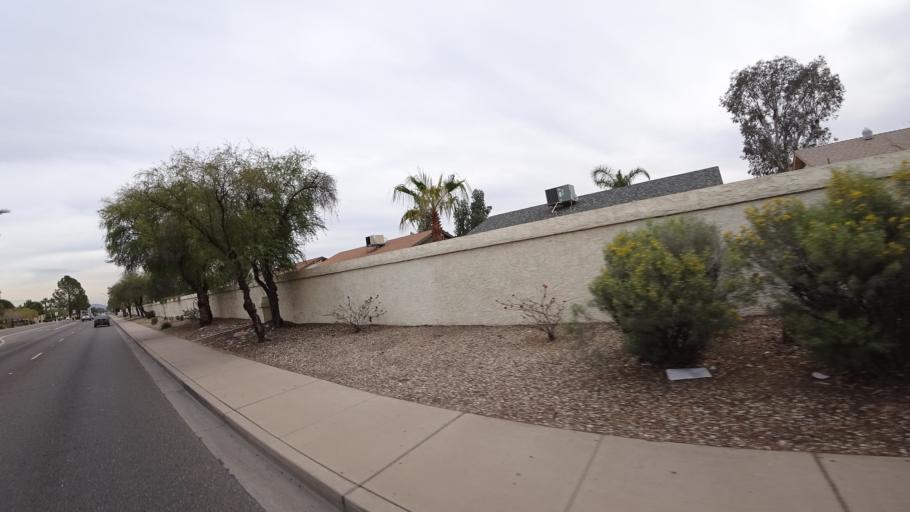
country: US
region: Arizona
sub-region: Maricopa County
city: Glendale
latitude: 33.5818
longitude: -112.1931
